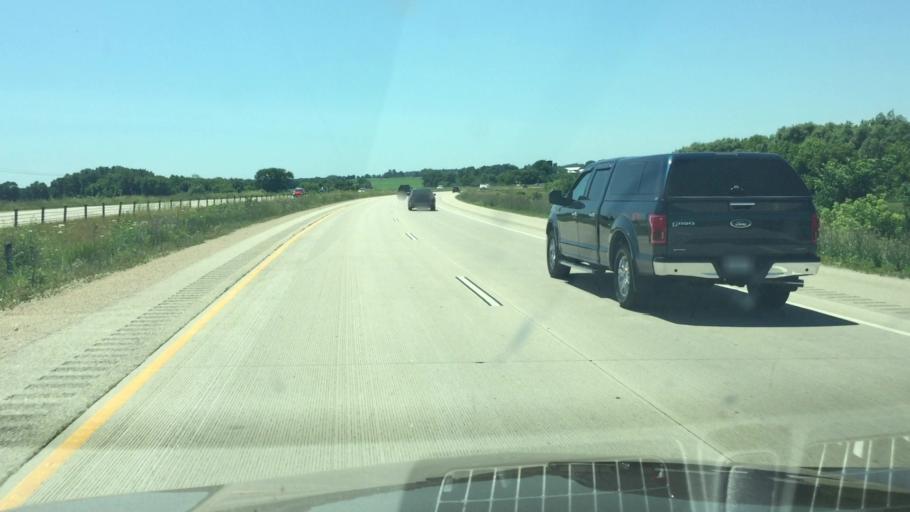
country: US
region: Wisconsin
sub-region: Dodge County
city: Beaver Dam
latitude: 43.4389
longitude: -88.8279
